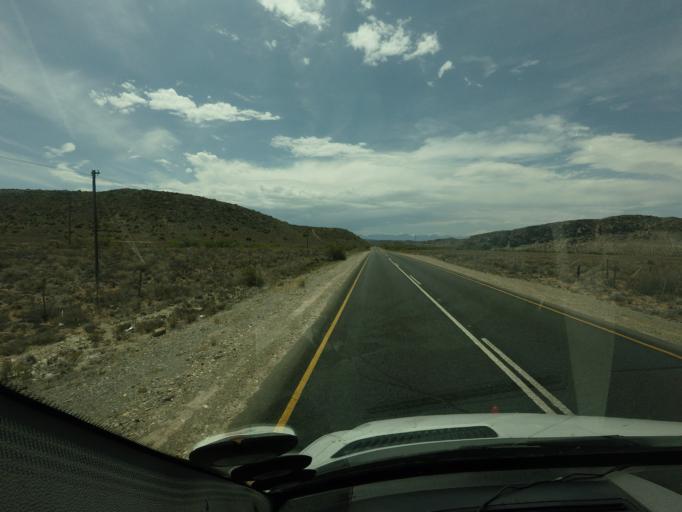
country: ZA
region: Western Cape
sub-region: Eden District Municipality
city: Ladismith
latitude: -33.7671
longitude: 20.9395
